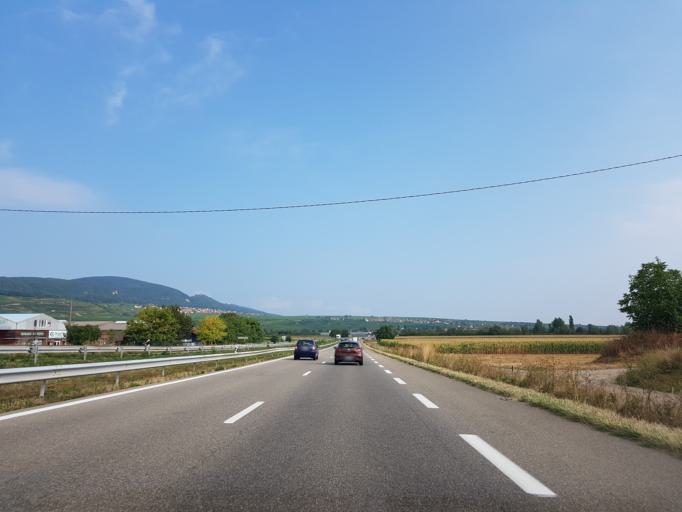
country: FR
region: Alsace
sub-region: Departement du Haut-Rhin
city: Pfaffenheim
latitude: 47.9915
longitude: 7.2940
